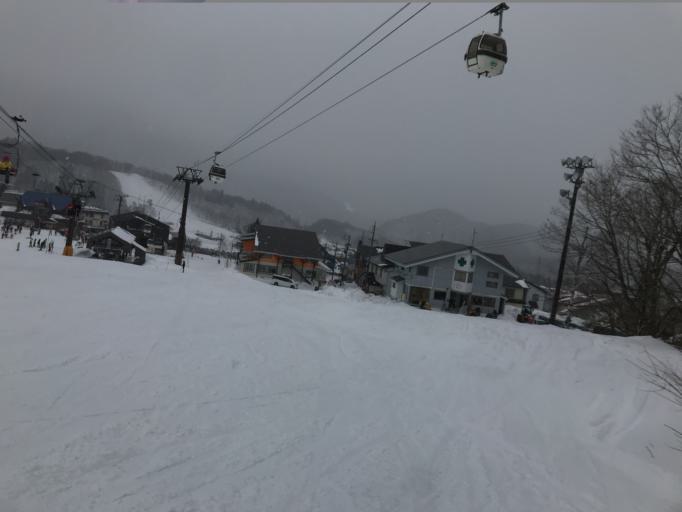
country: JP
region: Nagano
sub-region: Kitaazumi Gun
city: Hakuba
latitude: 36.7506
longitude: 137.8691
